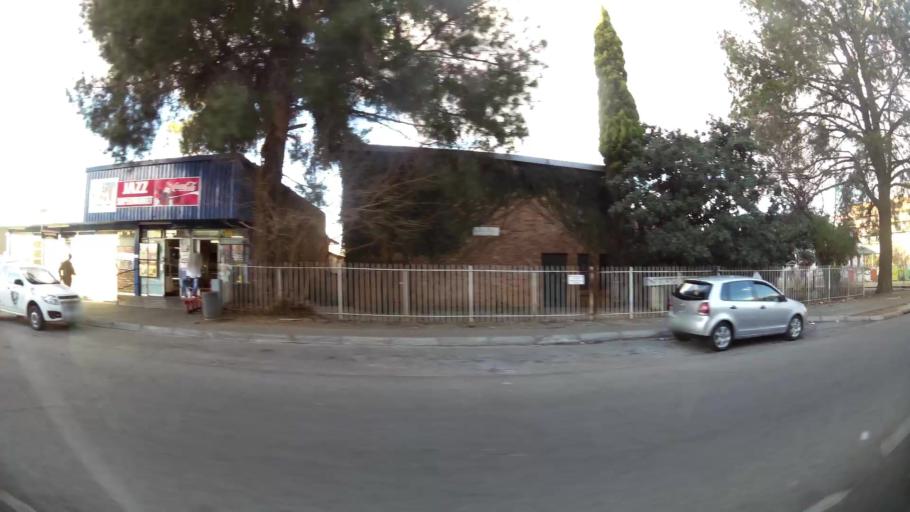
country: ZA
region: North-West
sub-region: Dr Kenneth Kaunda District Municipality
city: Potchefstroom
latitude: -26.7179
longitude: 27.0968
